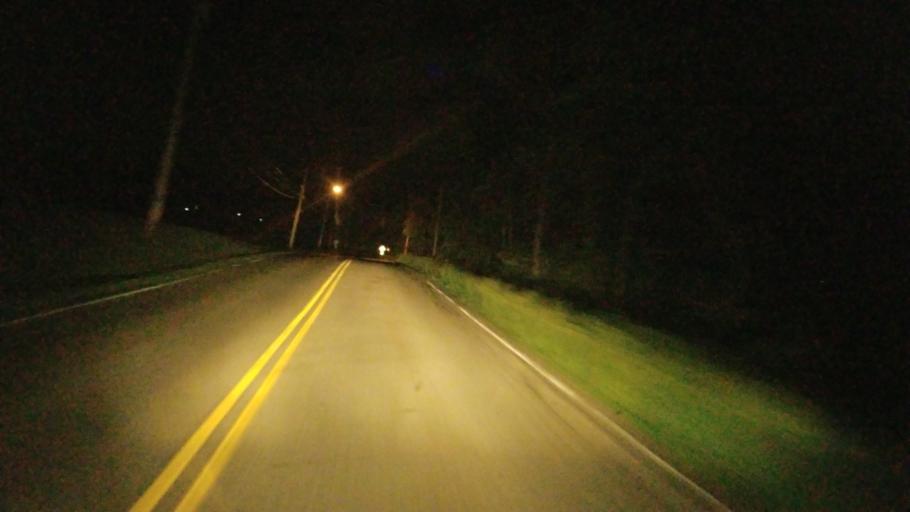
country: US
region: Ohio
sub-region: Trumbull County
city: McDonald
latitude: 41.1474
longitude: -80.7383
